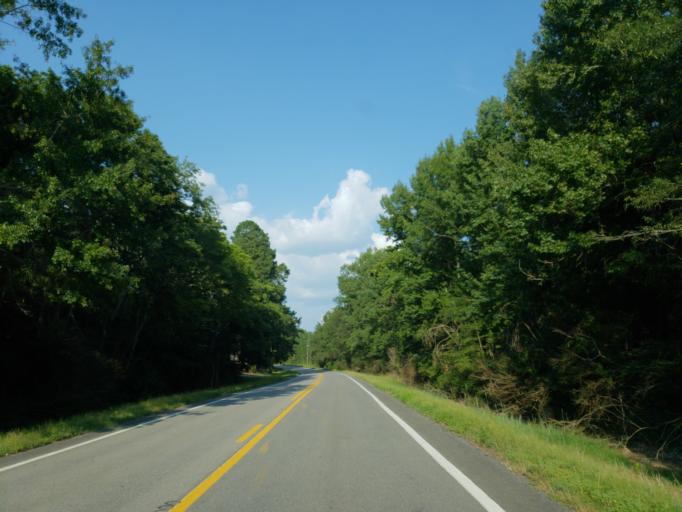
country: US
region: Alabama
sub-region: Greene County
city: Eutaw
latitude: 32.7585
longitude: -88.0148
